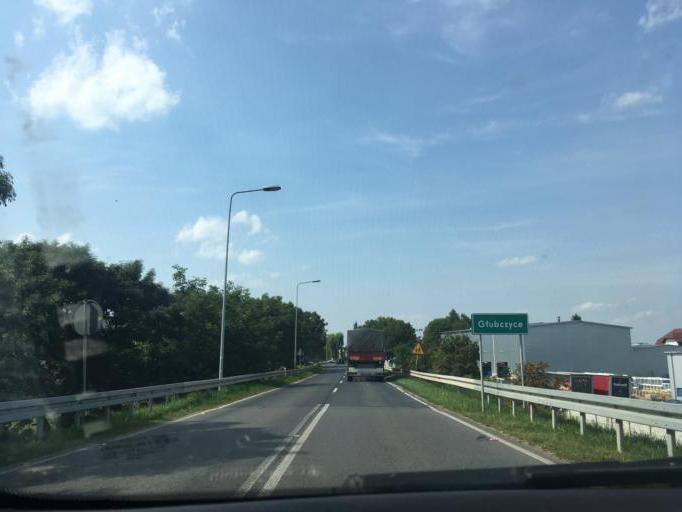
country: PL
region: Opole Voivodeship
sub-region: Powiat glubczycki
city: Glubczyce
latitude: 50.1932
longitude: 17.8442
